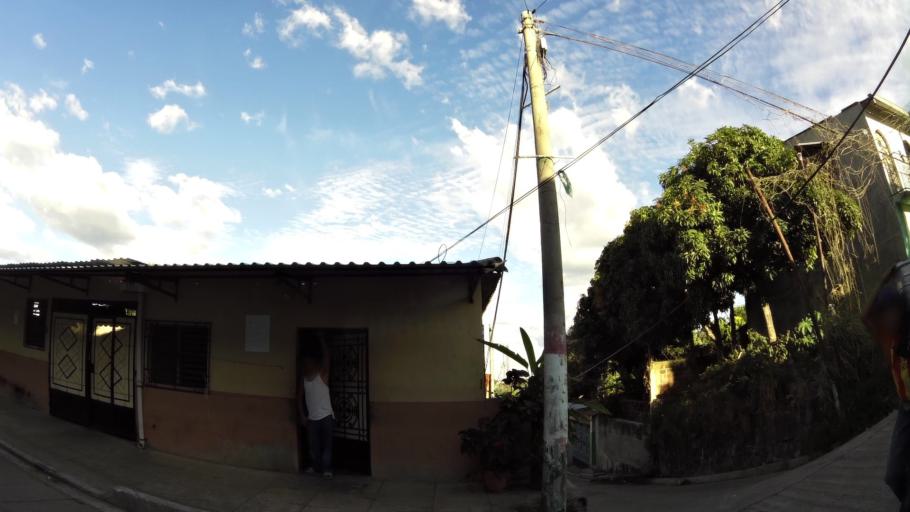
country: SV
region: Cuscatlan
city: Cojutepeque
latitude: 13.7128
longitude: -88.9326
